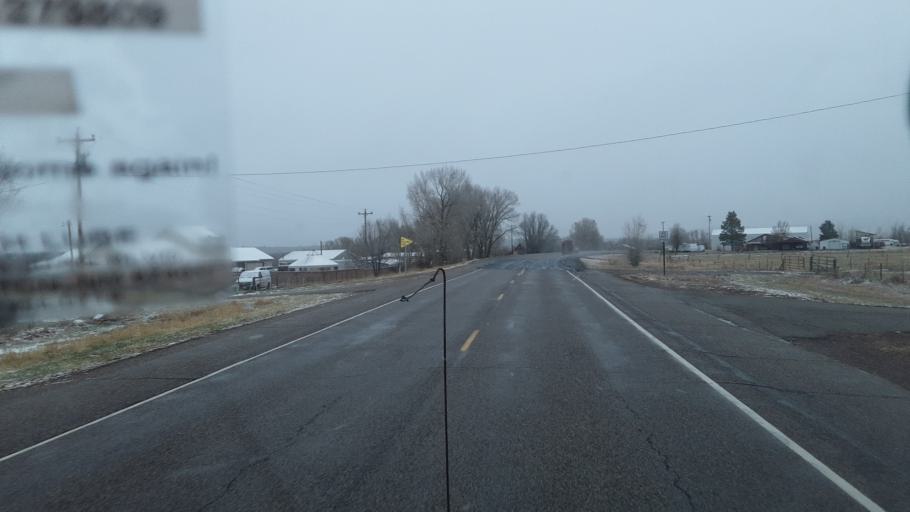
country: US
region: New Mexico
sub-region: Rio Arriba County
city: Tierra Amarilla
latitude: 36.7415
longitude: -106.5690
